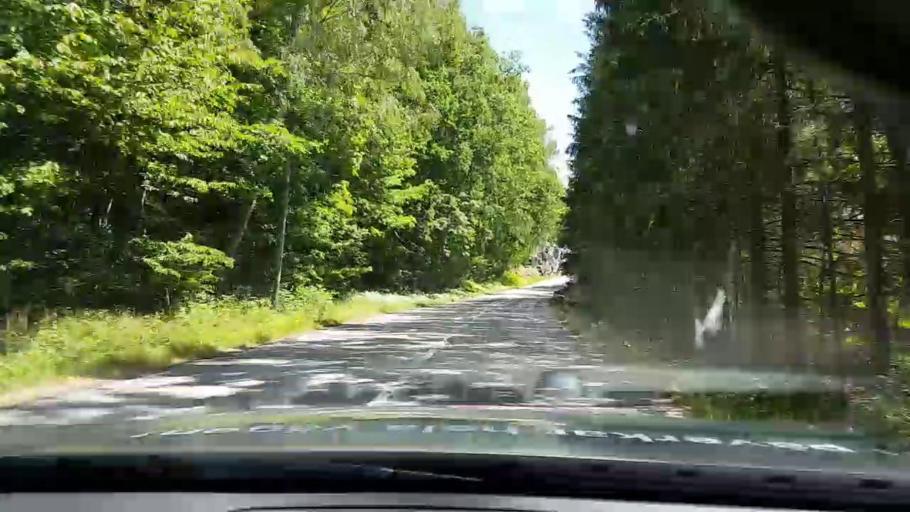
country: SE
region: Kalmar
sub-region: Vasterviks Kommun
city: Overum
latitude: 58.0727
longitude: 16.3720
